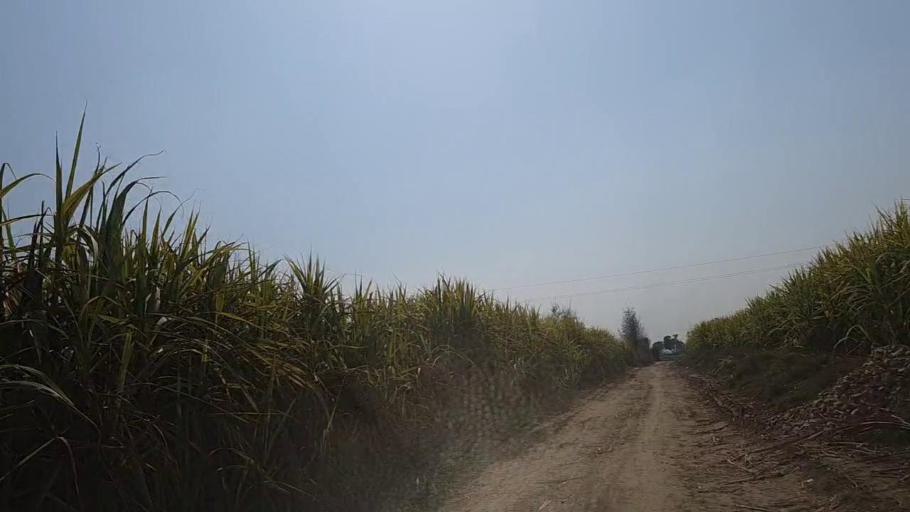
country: PK
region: Sindh
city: Moro
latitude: 26.6951
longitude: 67.9285
